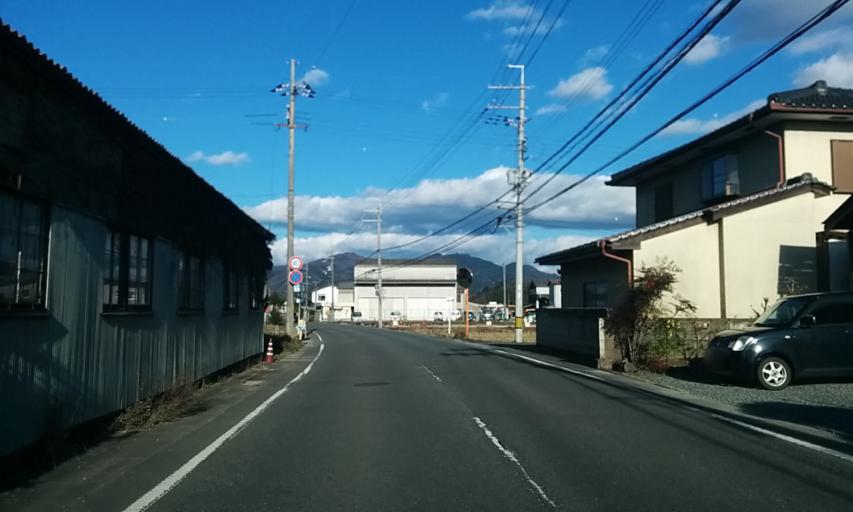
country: JP
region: Kyoto
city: Fukuchiyama
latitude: 35.2974
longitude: 135.0921
